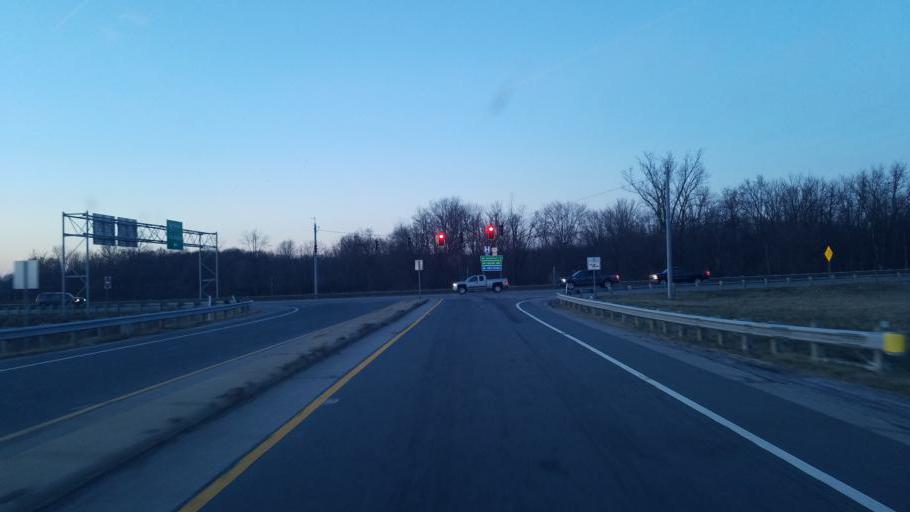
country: US
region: Ohio
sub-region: Ashland County
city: Ashland
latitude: 40.8567
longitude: -82.2613
